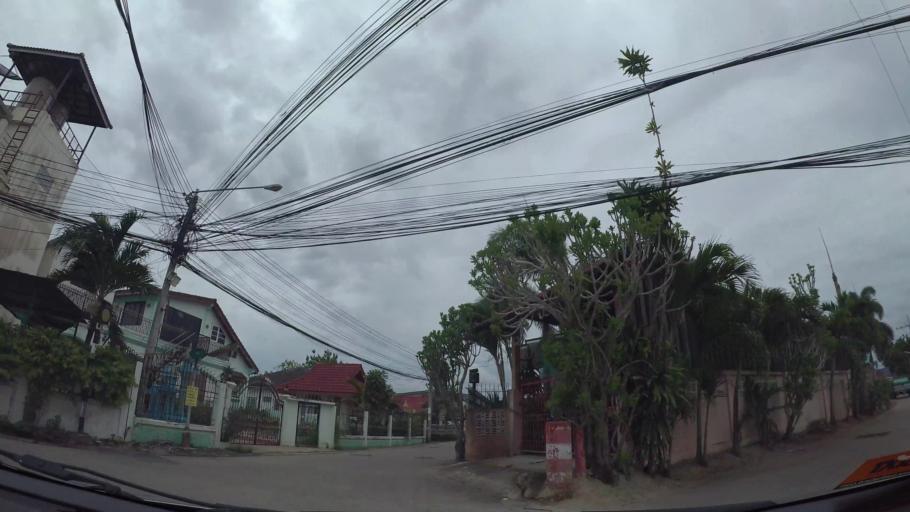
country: TH
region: Chon Buri
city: Sattahip
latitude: 12.7613
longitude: 100.8912
